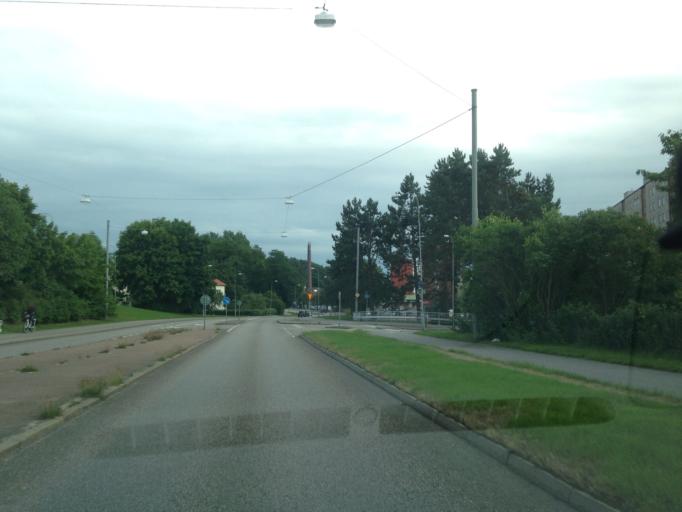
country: SE
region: Vaestra Goetaland
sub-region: Goteborg
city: Goeteborg
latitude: 57.7348
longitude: 11.9732
